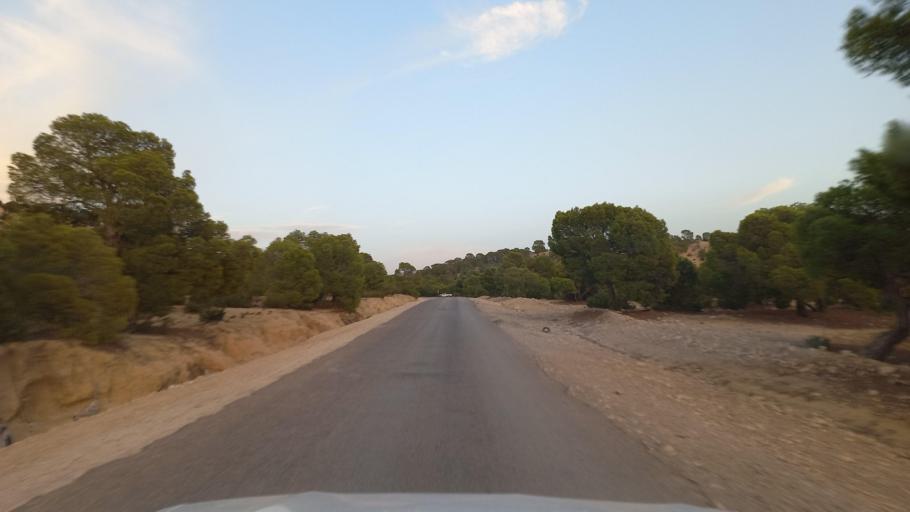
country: TN
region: Al Qasrayn
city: Sbiba
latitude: 35.4110
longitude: 8.9598
